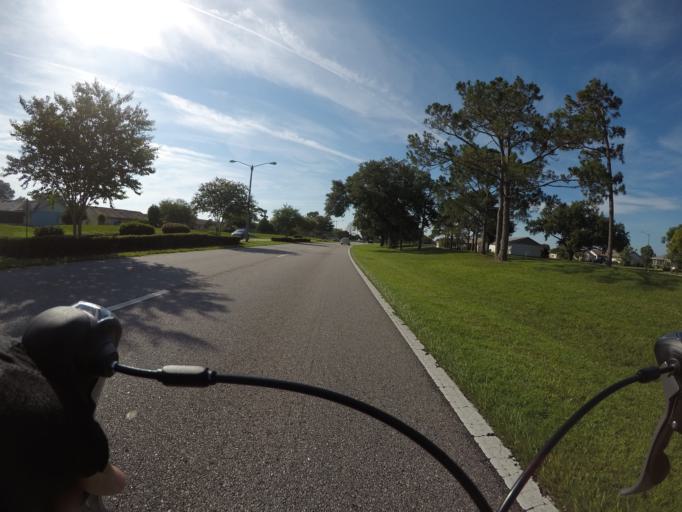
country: US
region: Florida
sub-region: Osceola County
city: Buenaventura Lakes
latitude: 28.3377
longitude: -81.3584
